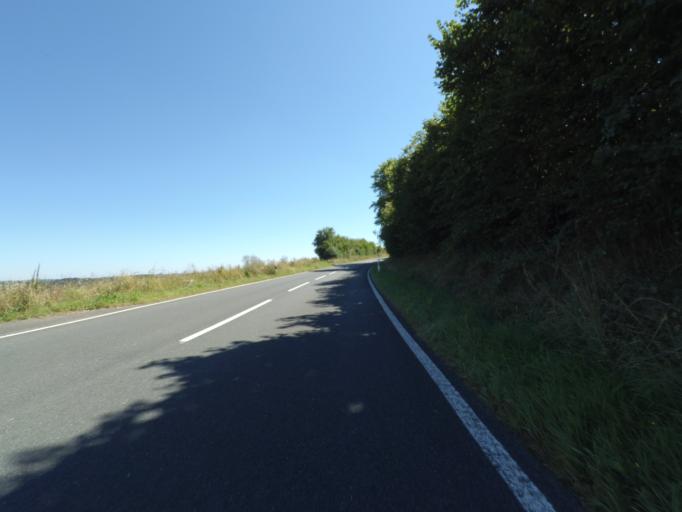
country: DE
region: Rheinland-Pfalz
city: Kliding
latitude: 50.1225
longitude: 7.0575
